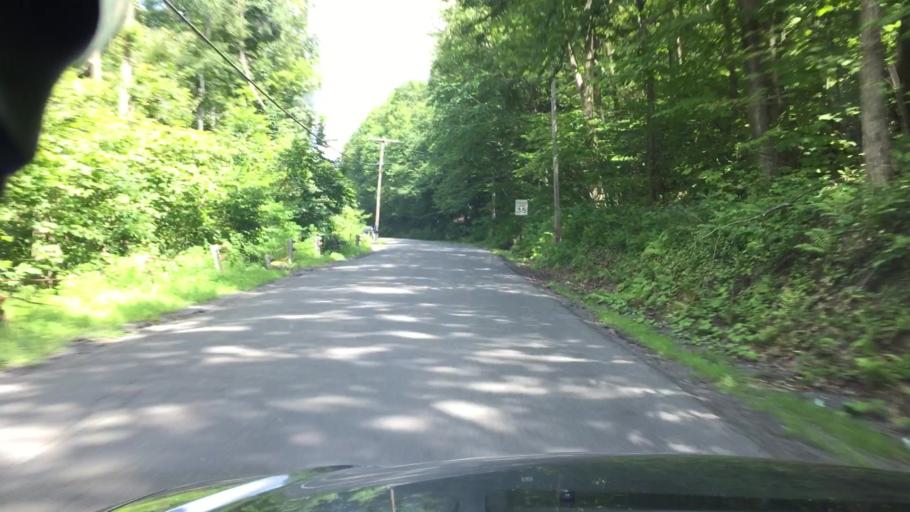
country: US
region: Pennsylvania
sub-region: Luzerne County
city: Oakdale
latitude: 41.0166
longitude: -75.9391
